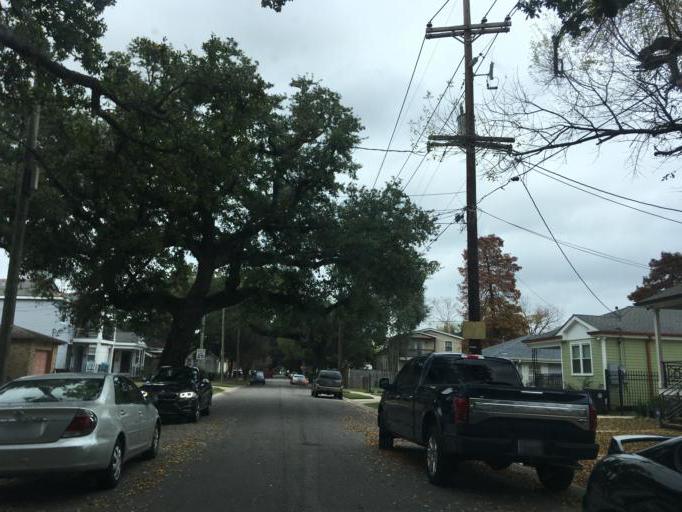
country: US
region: Louisiana
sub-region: Orleans Parish
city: New Orleans
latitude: 29.9928
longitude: -90.0624
